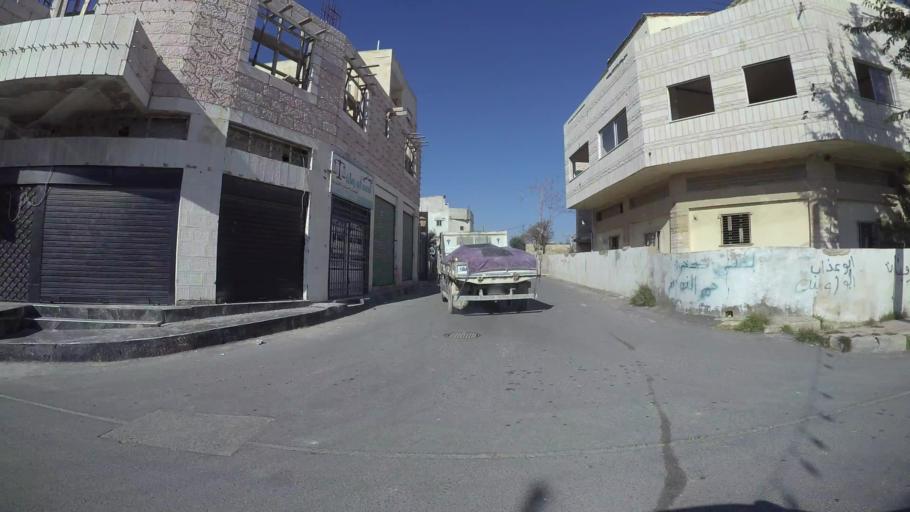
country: JO
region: Amman
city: Al Bunayyat ash Shamaliyah
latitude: 31.9075
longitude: 35.9058
